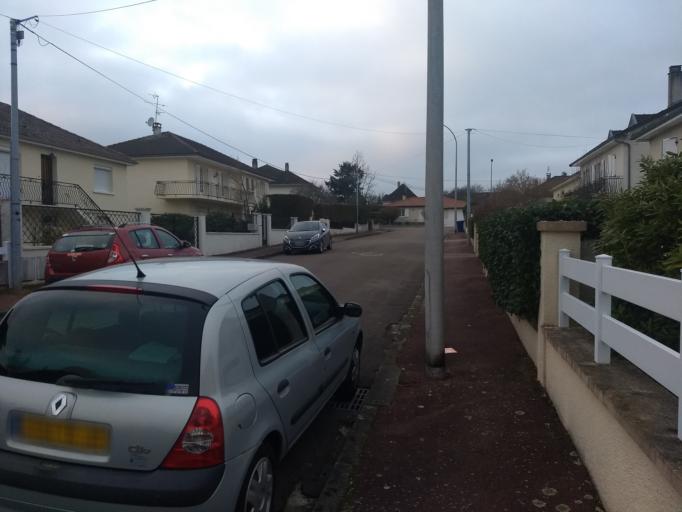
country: FR
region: Limousin
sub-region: Departement de la Haute-Vienne
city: Isle
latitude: 45.8251
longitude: 1.2036
